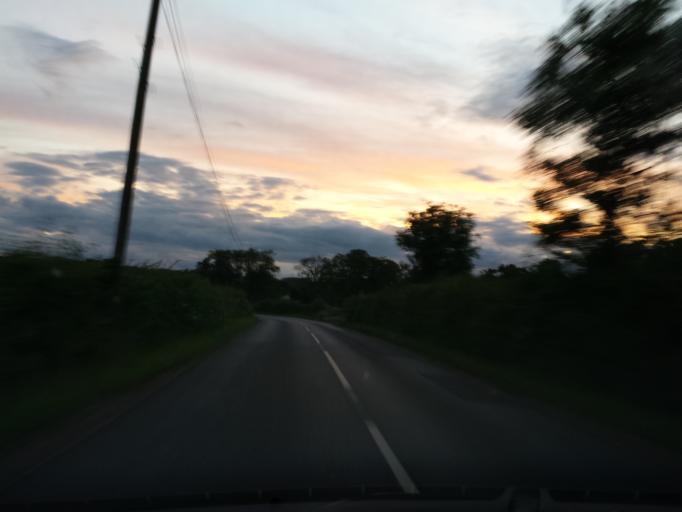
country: GB
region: Scotland
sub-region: The Scottish Borders
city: Eyemouth
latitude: 55.8829
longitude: -2.1476
